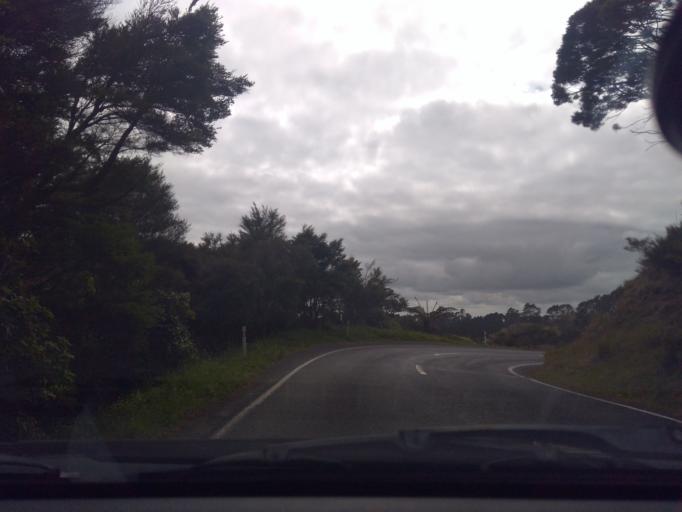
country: NZ
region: Auckland
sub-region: Auckland
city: Muriwai Beach
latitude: -36.8544
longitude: 174.4864
